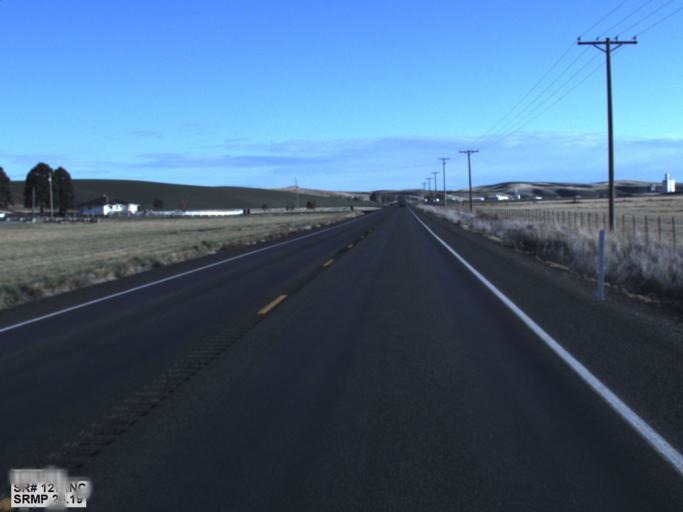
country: US
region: Washington
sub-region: Whitman County
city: Colfax
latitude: 46.8004
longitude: -117.6679
